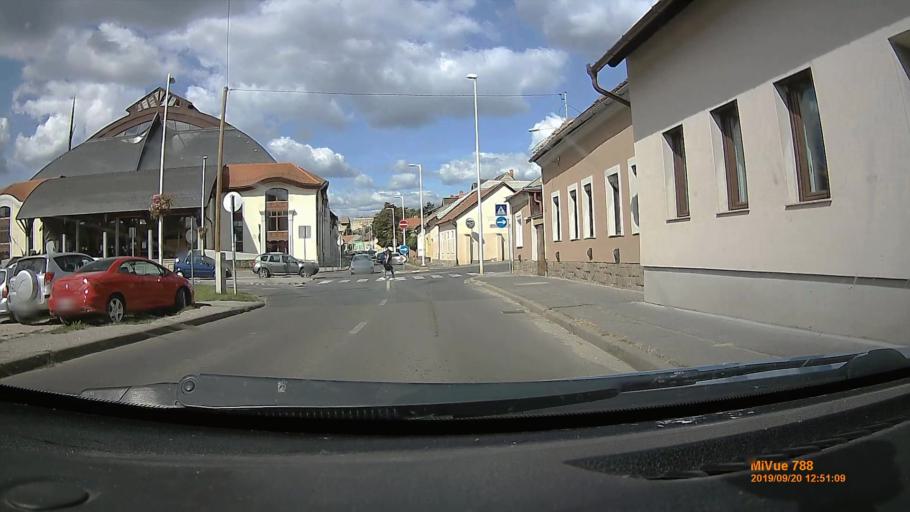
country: HU
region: Heves
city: Eger
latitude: 47.8989
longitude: 20.3846
